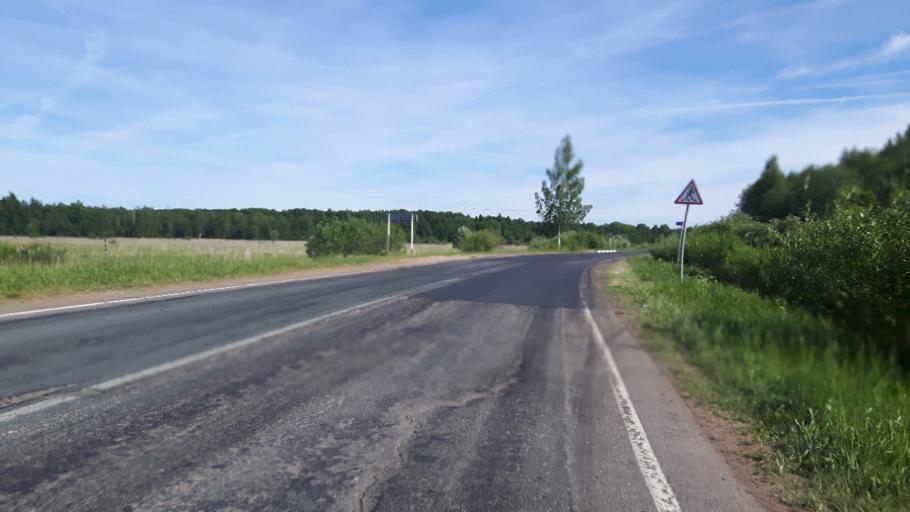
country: RU
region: Leningrad
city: Ivangorod
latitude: 59.4159
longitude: 28.3804
